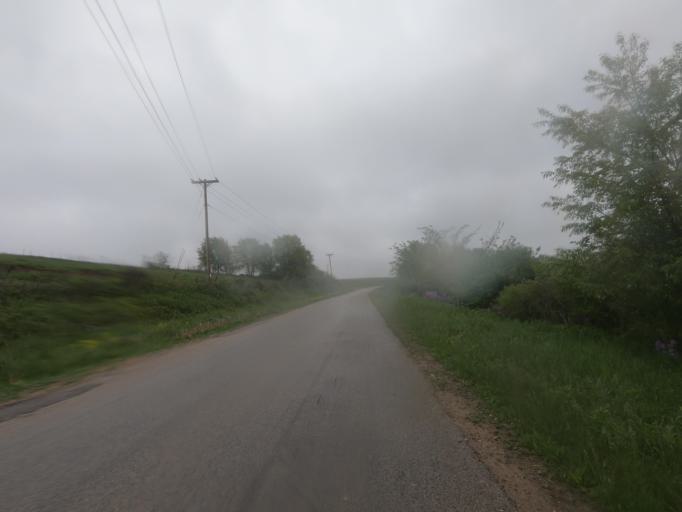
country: US
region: Wisconsin
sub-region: Grant County
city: Hazel Green
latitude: 42.5096
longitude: -90.4668
